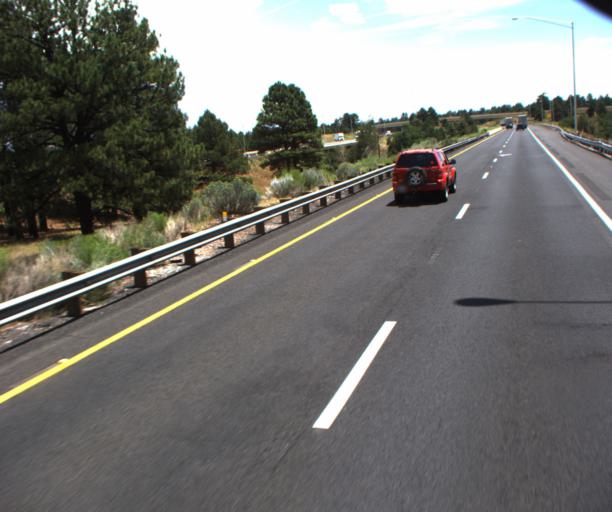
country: US
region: Arizona
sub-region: Coconino County
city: Flagstaff
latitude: 35.1734
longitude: -111.6673
